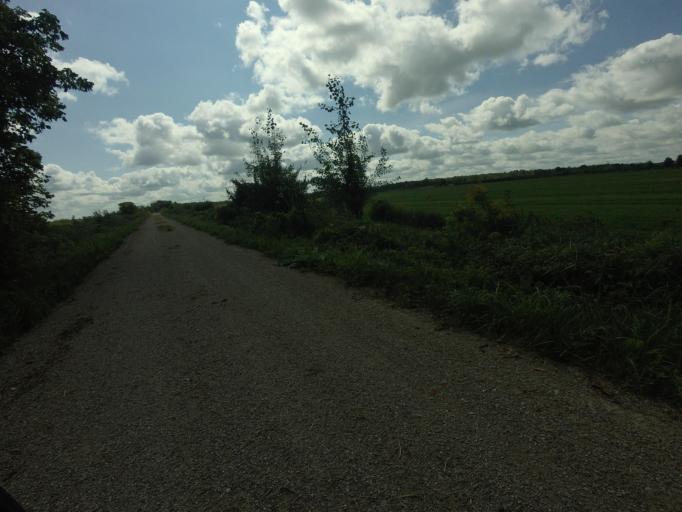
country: CA
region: Ontario
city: Huron East
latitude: 43.6422
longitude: -81.2074
